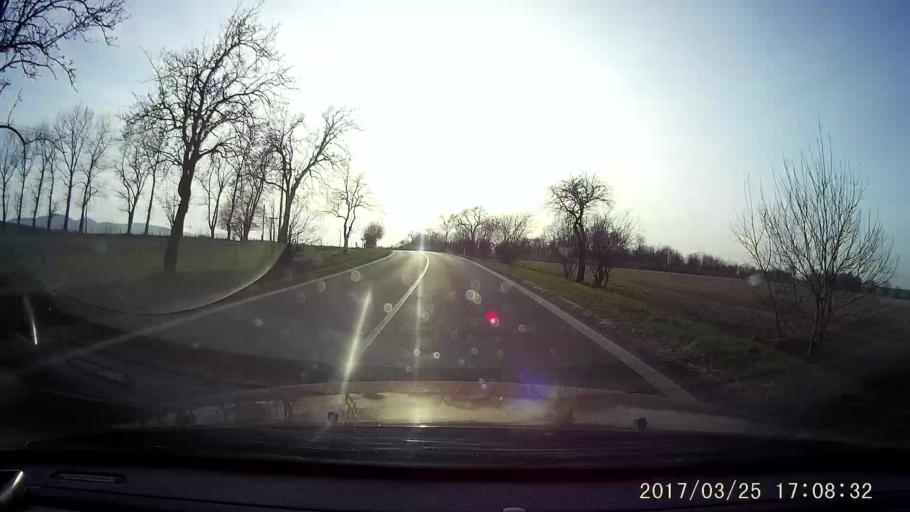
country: CZ
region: Liberecky
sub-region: Okres Liberec
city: Hejnice
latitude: 50.9339
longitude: 15.1685
